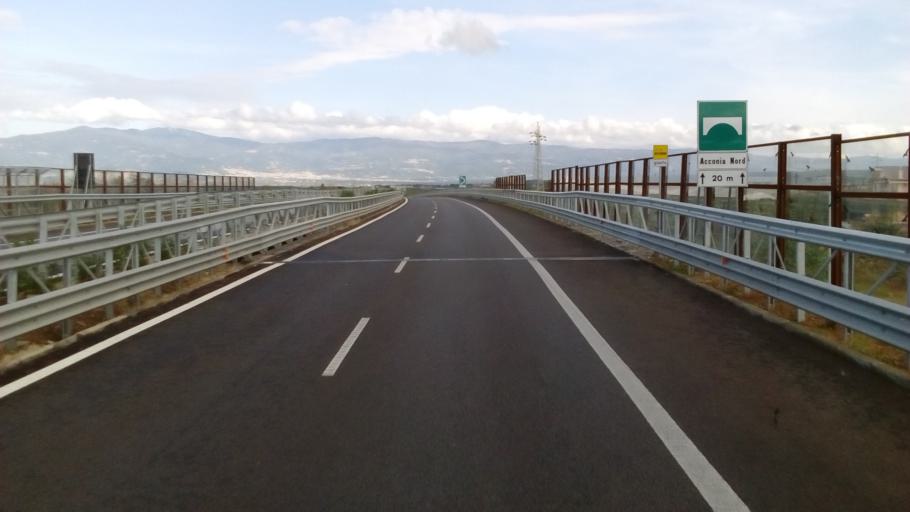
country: IT
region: Calabria
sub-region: Provincia di Catanzaro
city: Acconia
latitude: 38.8393
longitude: 16.2615
